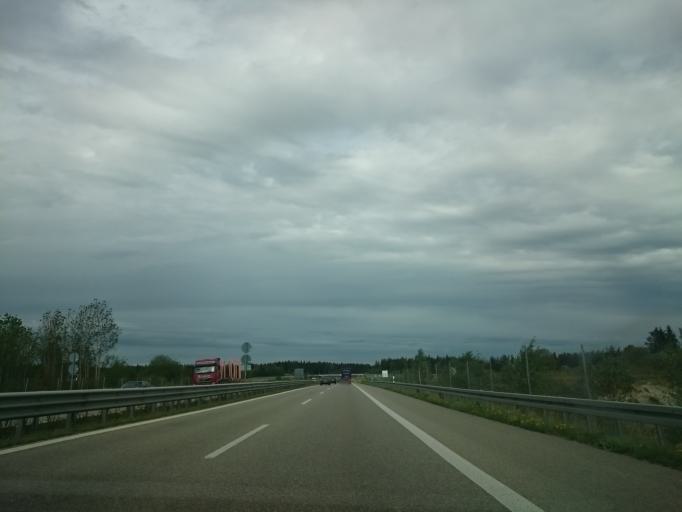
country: DE
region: Bavaria
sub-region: Upper Bavaria
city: Landsberg am Lech
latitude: 48.0556
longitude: 10.8333
